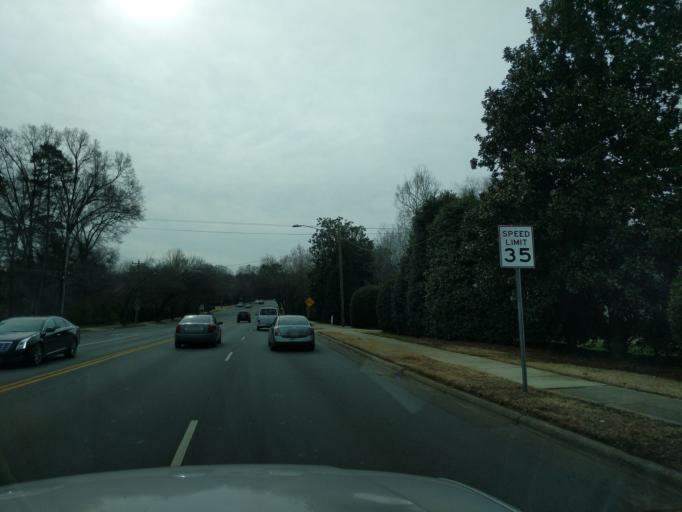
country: US
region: North Carolina
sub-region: Mecklenburg County
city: Charlotte
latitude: 35.1718
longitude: -80.8230
